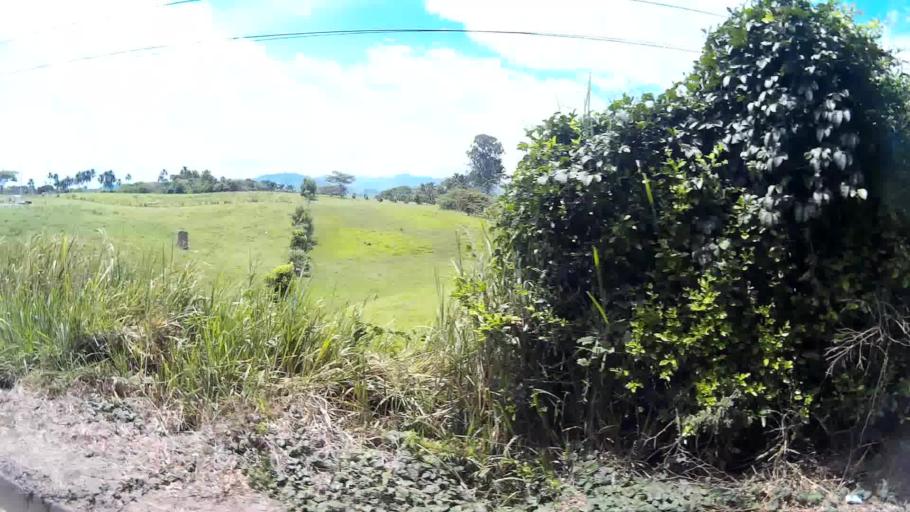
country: CO
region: Risaralda
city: La Virginia
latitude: 4.8207
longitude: -75.8409
